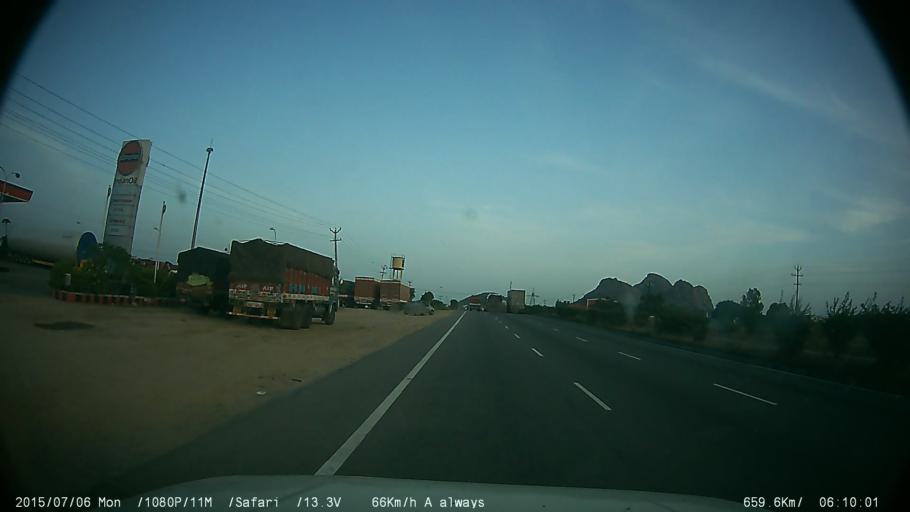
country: IN
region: Tamil Nadu
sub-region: Krishnagiri
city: Kelamangalam
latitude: 12.6499
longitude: 78.0357
